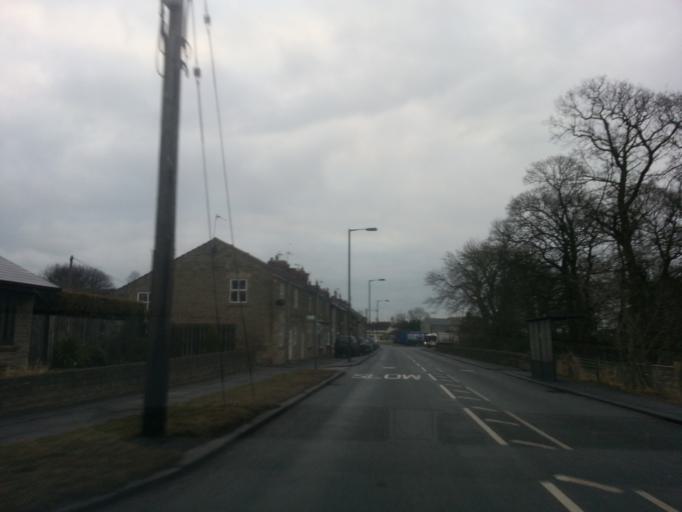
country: GB
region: England
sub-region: County Durham
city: Hamsterley
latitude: 54.7051
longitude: -1.7842
